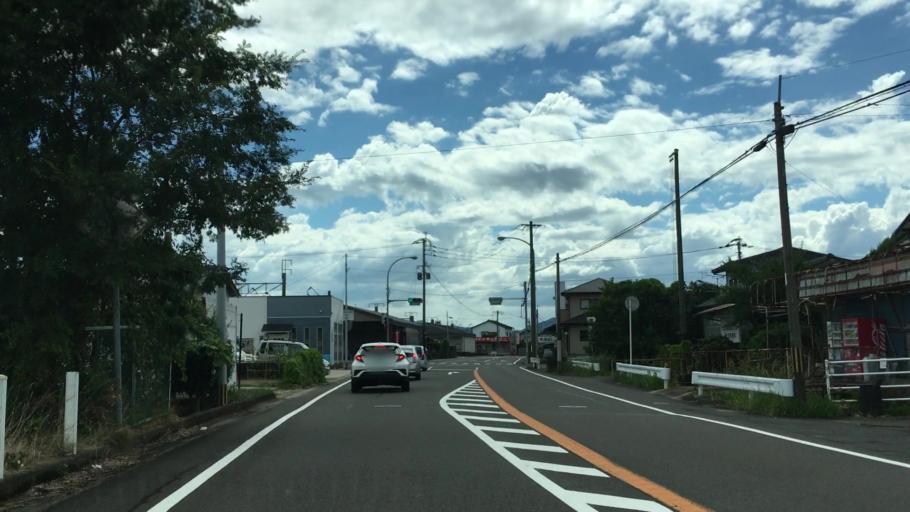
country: JP
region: Saga Prefecture
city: Saga-shi
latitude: 33.2207
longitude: 130.1697
